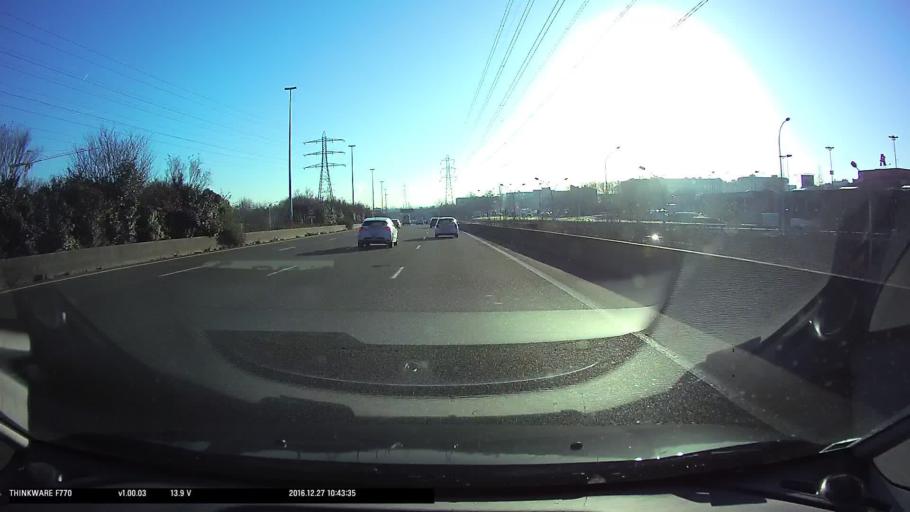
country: FR
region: Ile-de-France
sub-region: Departement du Val-d'Oise
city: Cergy-Pontoise
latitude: 49.0404
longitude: 2.0822
